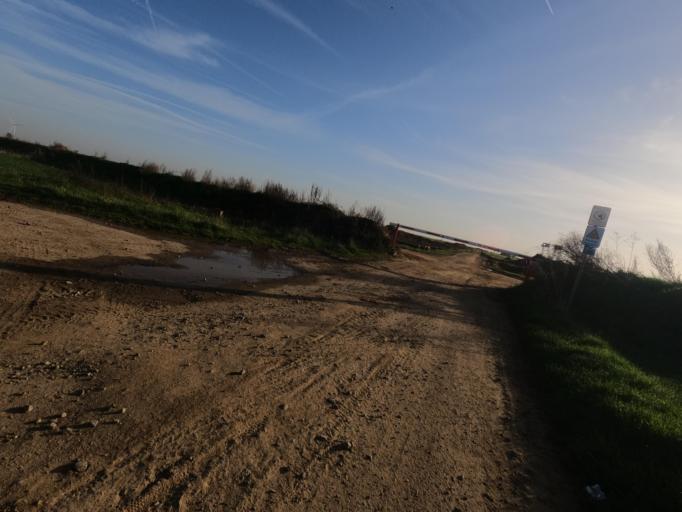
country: DE
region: North Rhine-Westphalia
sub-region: Regierungsbezirk Koln
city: Titz
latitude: 51.0691
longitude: 6.4145
